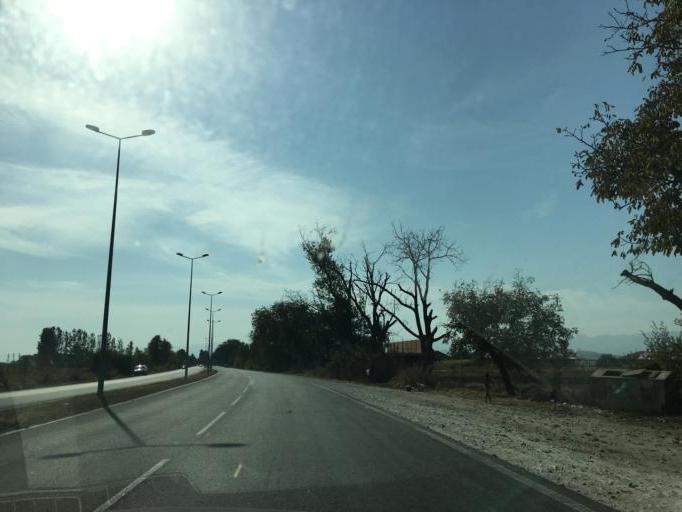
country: BG
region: Pazardzhik
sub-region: Obshtina Pazardzhik
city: Pazardzhik
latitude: 42.2212
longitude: 24.3116
